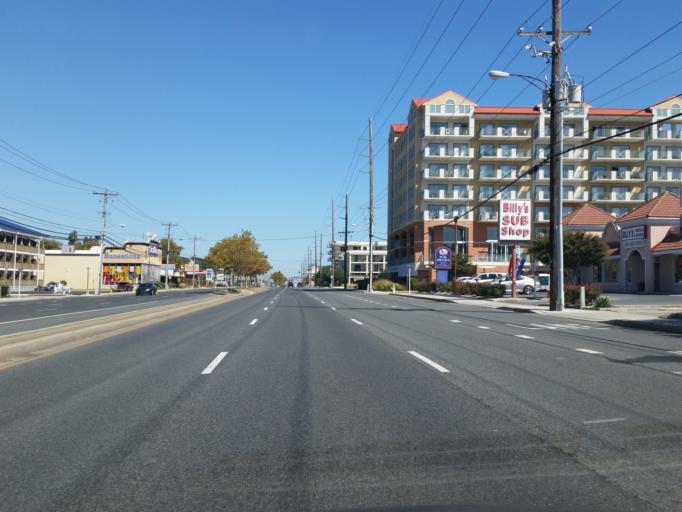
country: US
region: Delaware
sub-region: Sussex County
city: Bethany Beach
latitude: 38.4446
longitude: -75.0529
